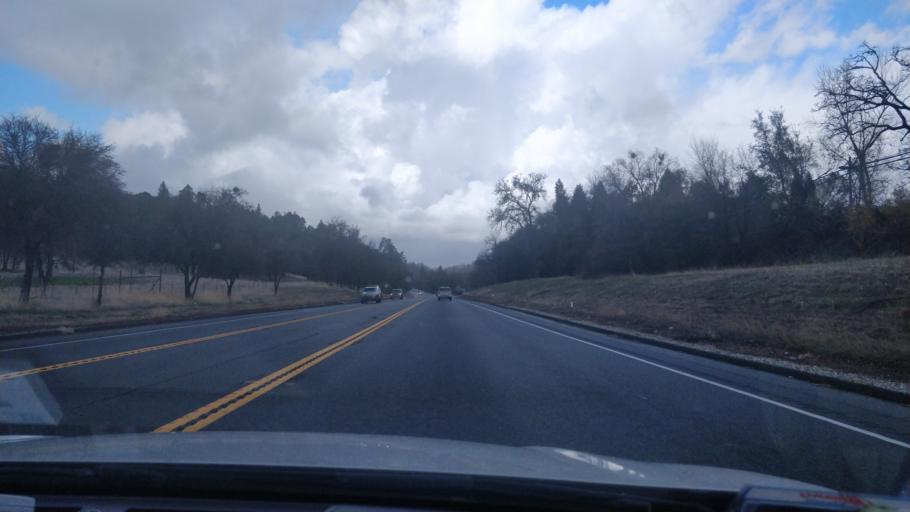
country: US
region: California
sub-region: Nevada County
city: Lake of the Pines
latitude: 39.0694
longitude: -121.0874
